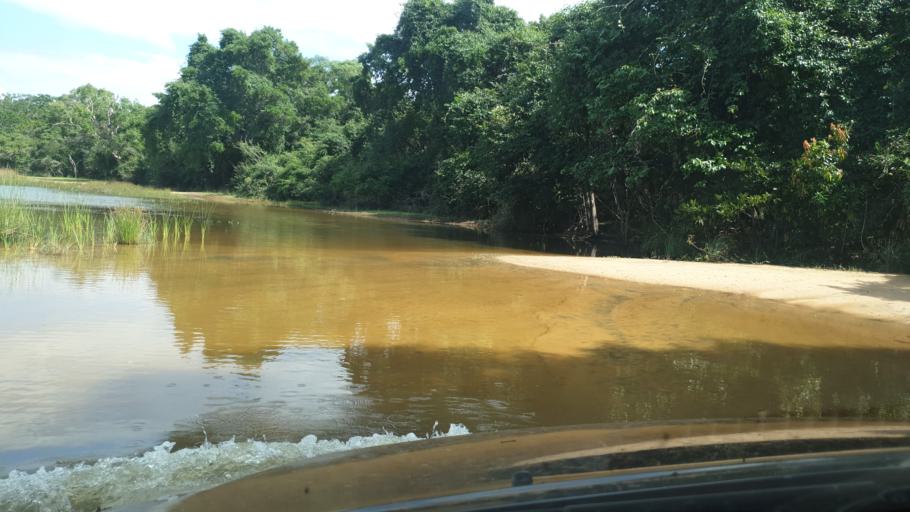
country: LK
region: North Central
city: Anuradhapura
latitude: 8.4241
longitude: 80.0117
